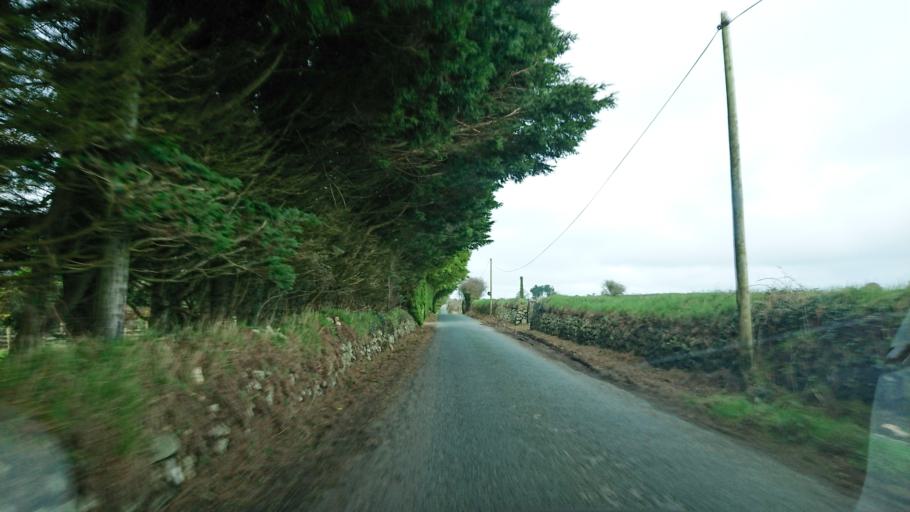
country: IE
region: Munster
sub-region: Waterford
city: Portlaw
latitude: 52.1657
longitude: -7.3057
